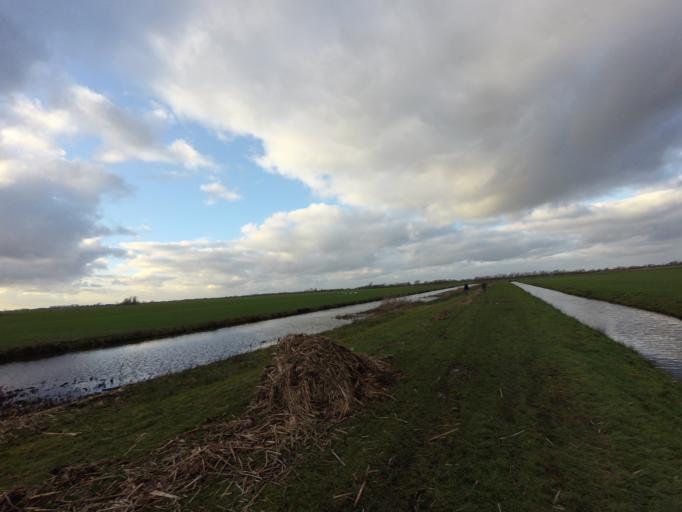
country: NL
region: Utrecht
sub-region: Gemeente Lopik
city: Lopik
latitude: 52.0053
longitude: 4.9242
